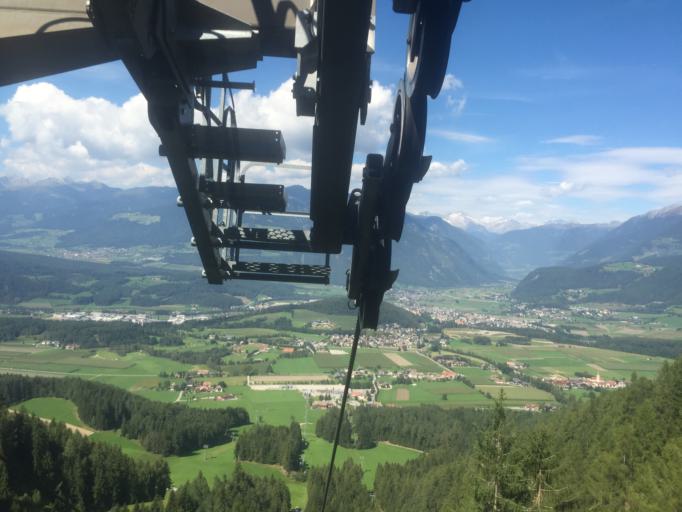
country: IT
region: Trentino-Alto Adige
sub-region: Bolzano
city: Riscone
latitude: 46.7599
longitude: 11.9468
